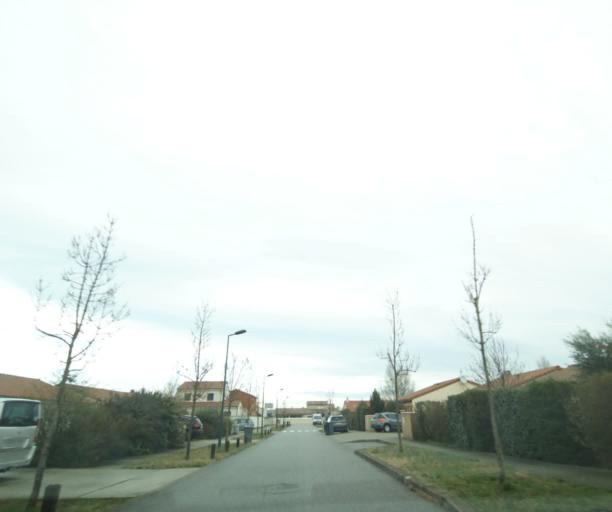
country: FR
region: Rhone-Alpes
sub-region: Departement de la Drome
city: Bourg-les-Valence
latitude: 44.9559
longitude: 4.8854
